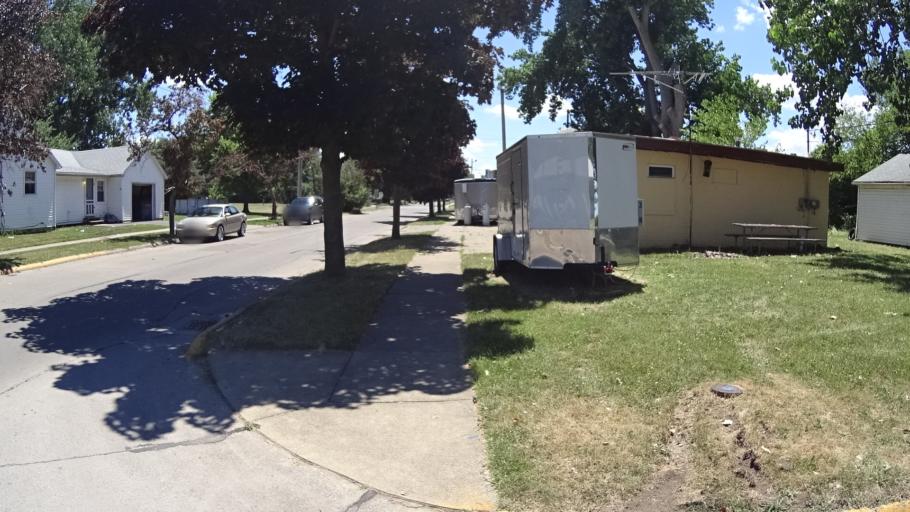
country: US
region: Ohio
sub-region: Erie County
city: Sandusky
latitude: 41.4485
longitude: -82.6828
